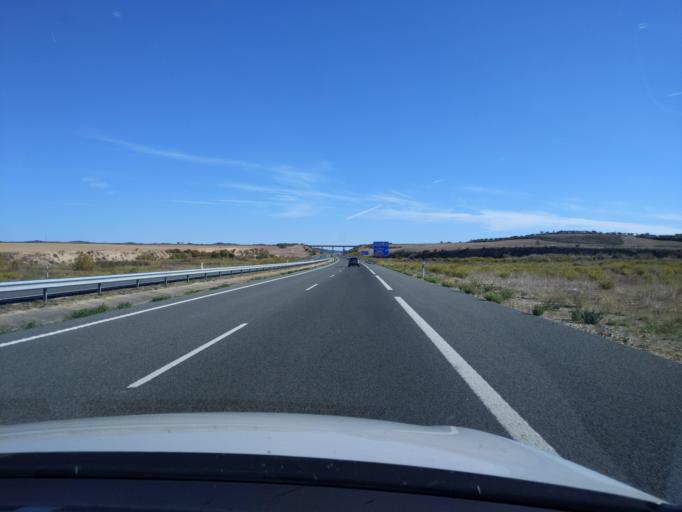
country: ES
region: Navarre
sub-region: Provincia de Navarra
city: Los Arcos
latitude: 42.5490
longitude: -2.1968
